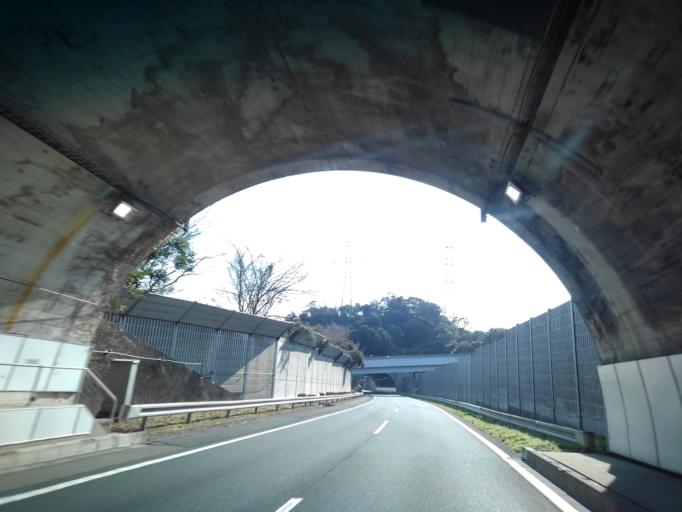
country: JP
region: Kanagawa
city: Zushi
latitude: 35.3271
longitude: 139.5960
